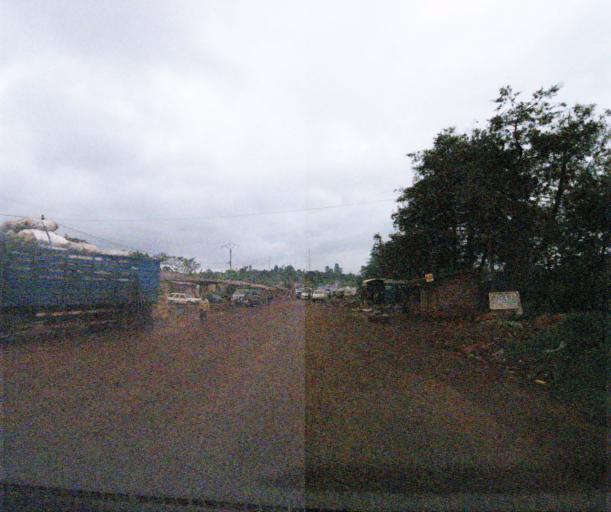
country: CM
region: West
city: Bansoa
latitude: 5.5009
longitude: 10.2399
